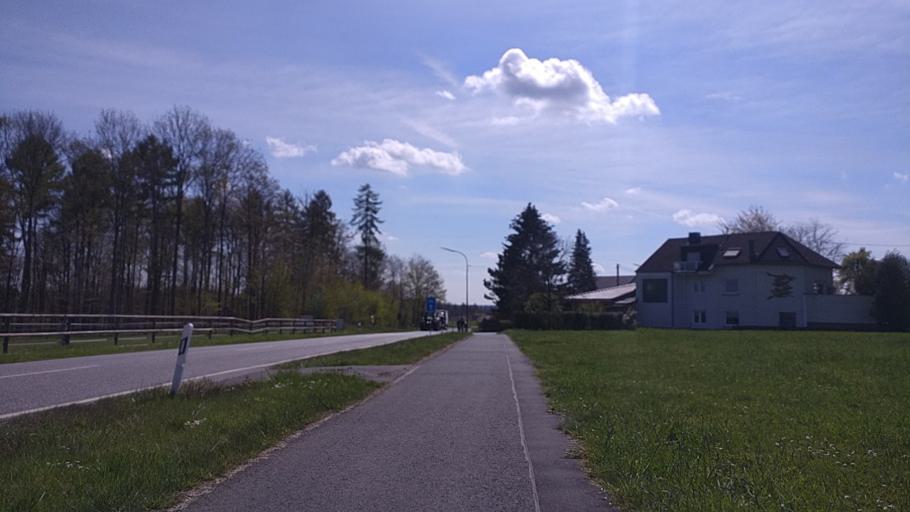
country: DE
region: Rheinland-Pfalz
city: Asbach
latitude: 50.6571
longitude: 7.4353
